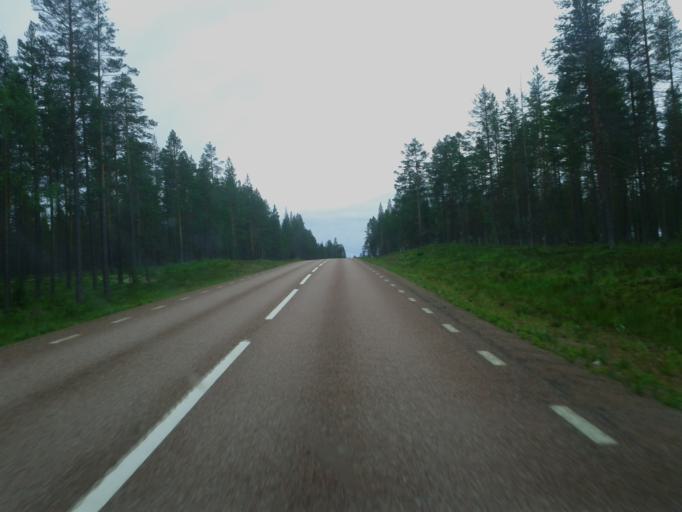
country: SE
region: Dalarna
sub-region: Alvdalens Kommun
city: AElvdalen
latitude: 61.4817
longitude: 13.4235
